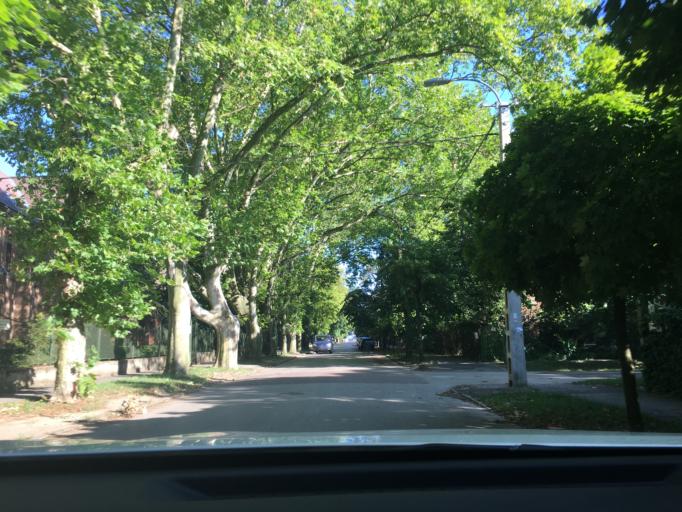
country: HU
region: Budapest
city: Budapest XVI. keruelet
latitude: 47.5081
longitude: 19.1965
